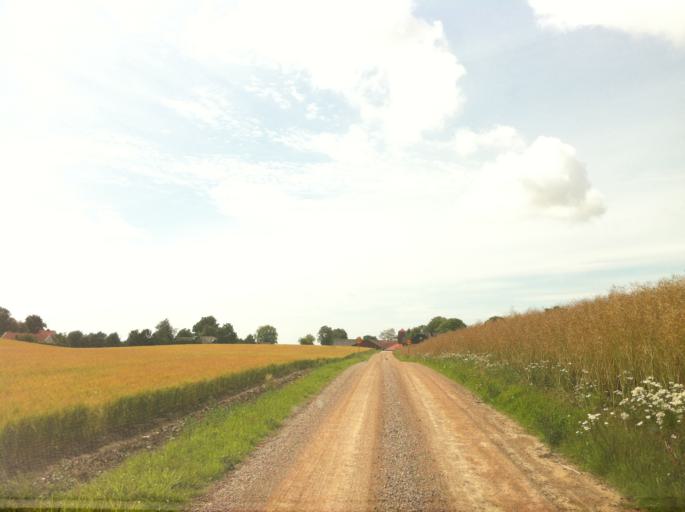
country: SE
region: Skane
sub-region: Skurups Kommun
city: Skurup
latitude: 55.4520
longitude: 13.4317
